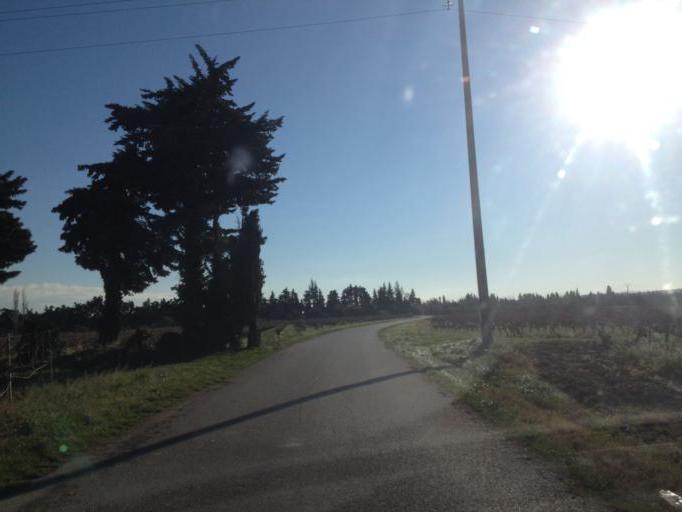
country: FR
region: Provence-Alpes-Cote d'Azur
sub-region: Departement du Vaucluse
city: Courthezon
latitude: 44.0888
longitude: 4.9099
